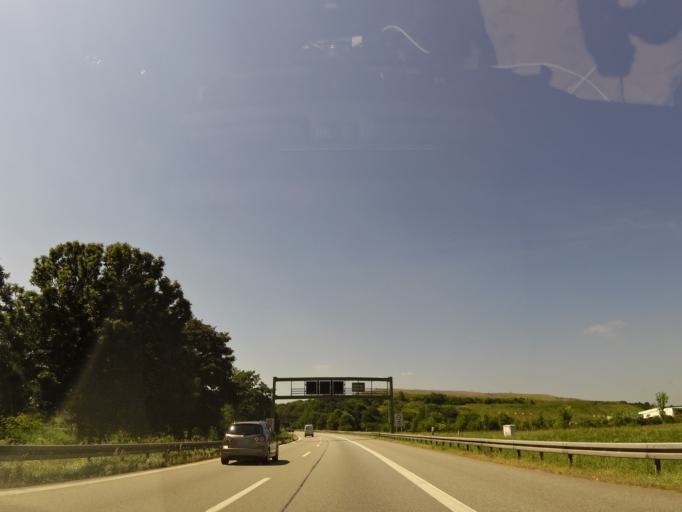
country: DE
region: Bavaria
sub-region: Upper Bavaria
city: Garching bei Munchen
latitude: 48.2292
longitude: 11.6324
